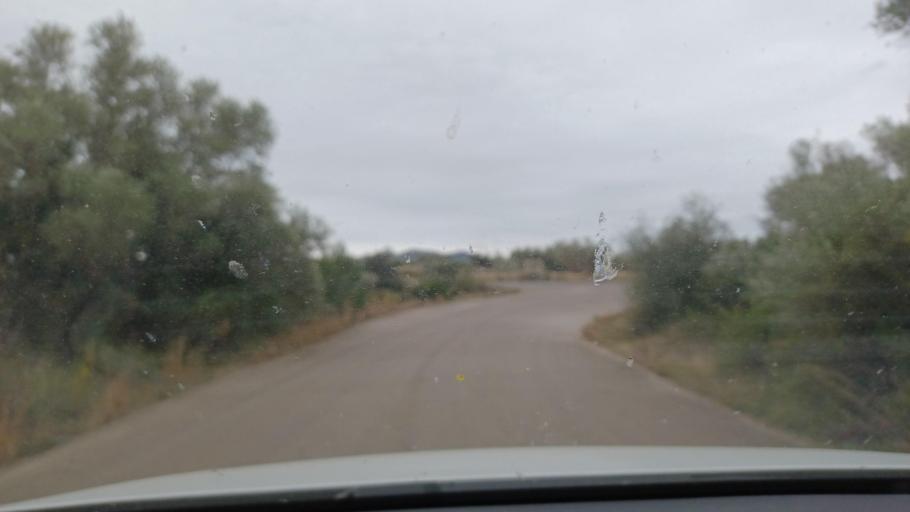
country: ES
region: Valencia
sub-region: Provincia de Castello
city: Canet lo Roig
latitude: 40.5828
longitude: 0.2841
